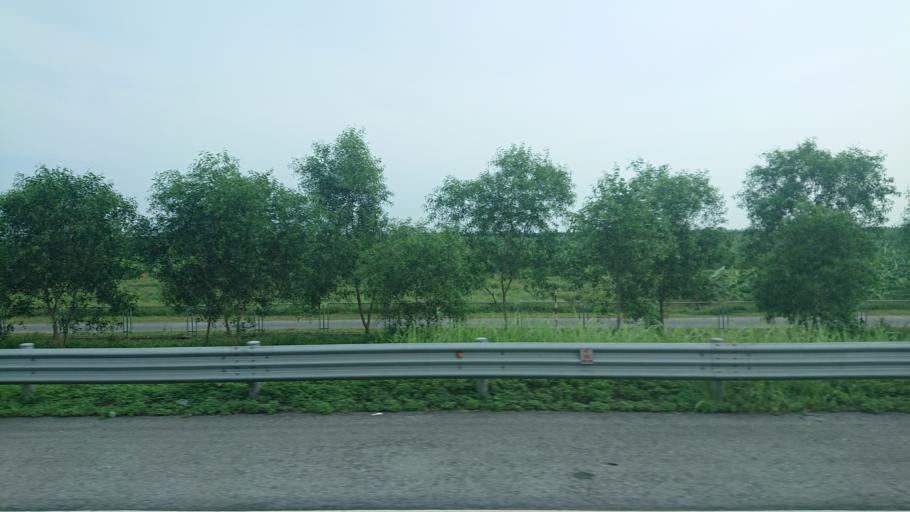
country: VN
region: Hai Duong
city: Tu Ky
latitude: 20.8275
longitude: 106.4573
